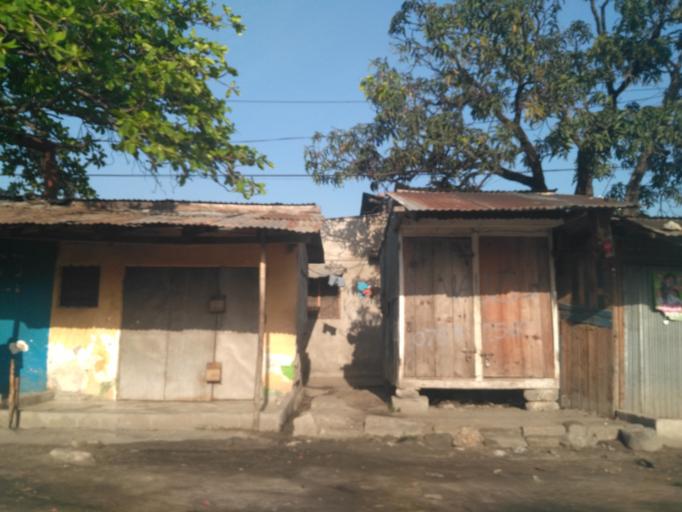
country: TZ
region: Dar es Salaam
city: Magomeni
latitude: -6.7873
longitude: 39.2653
